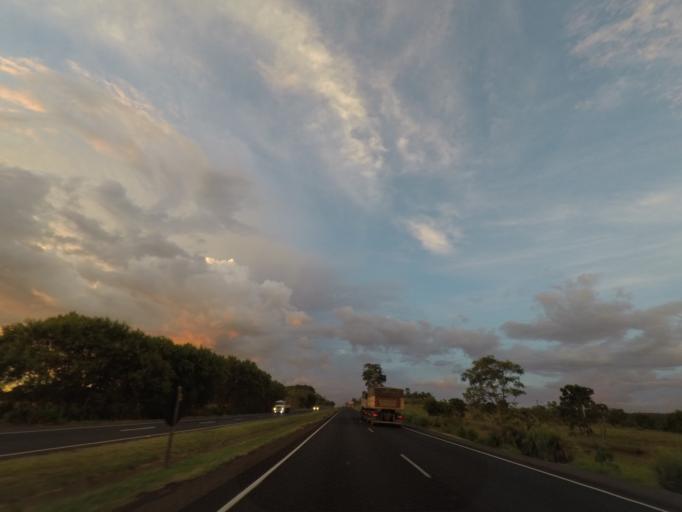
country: BR
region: Minas Gerais
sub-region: Uberaba
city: Uberaba
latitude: -19.5986
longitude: -48.0258
